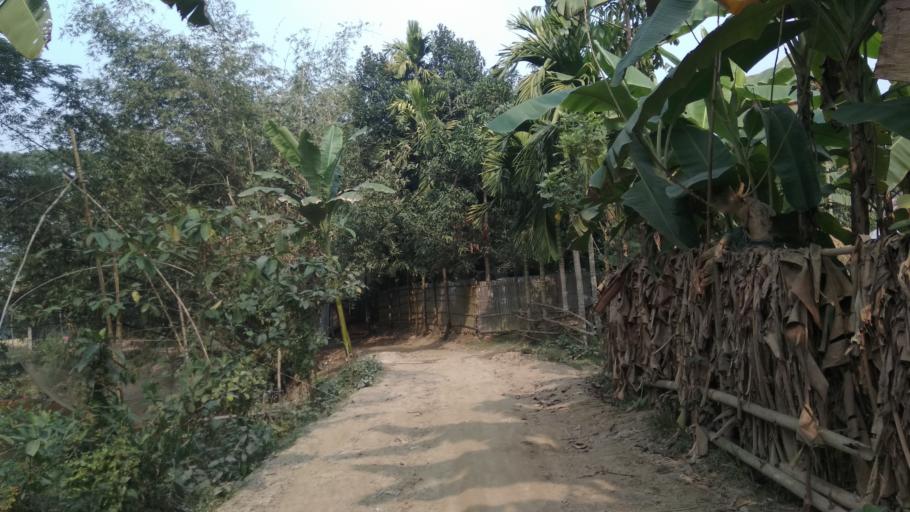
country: BD
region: Dhaka
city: Netrakona
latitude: 24.8914
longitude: 90.6651
